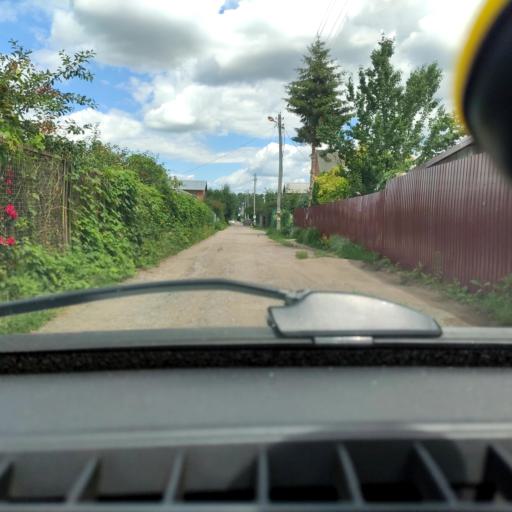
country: RU
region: Samara
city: Podstepki
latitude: 53.6031
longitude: 49.2259
